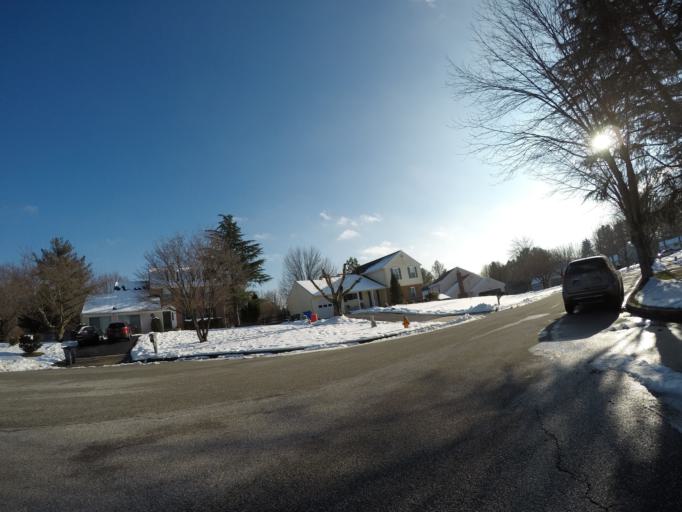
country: US
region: Maryland
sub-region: Howard County
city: Ellicott City
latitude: 39.2418
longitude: -76.8052
